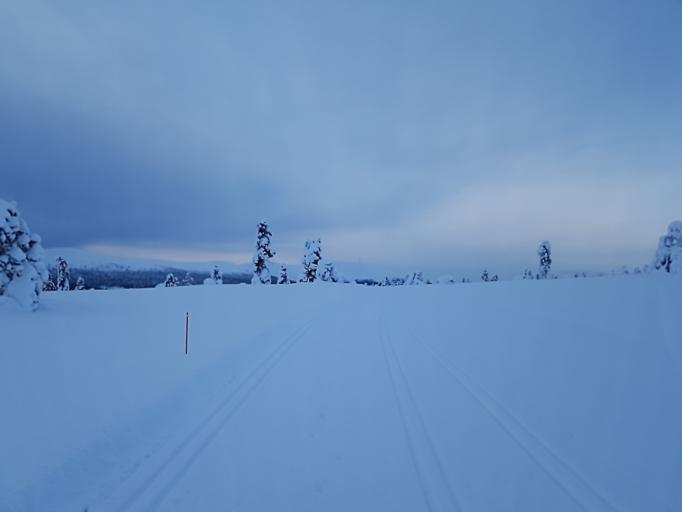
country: FI
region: Lapland
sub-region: Tunturi-Lappi
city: Kolari
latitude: 67.6572
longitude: 24.2289
